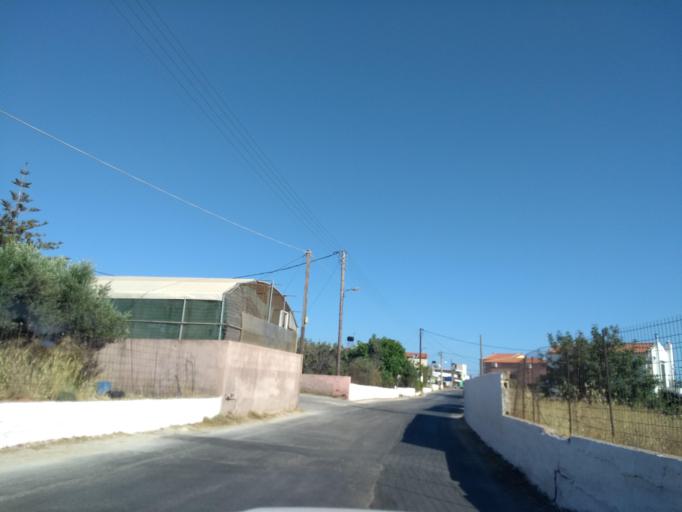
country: GR
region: Crete
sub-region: Nomos Chanias
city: Pithari
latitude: 35.5630
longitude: 24.0921
